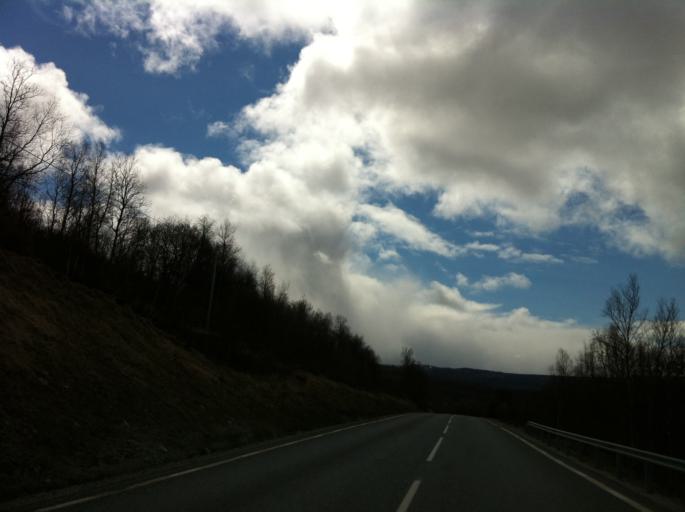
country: NO
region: Sor-Trondelag
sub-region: Tydal
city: Aas
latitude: 62.6702
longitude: 12.4297
